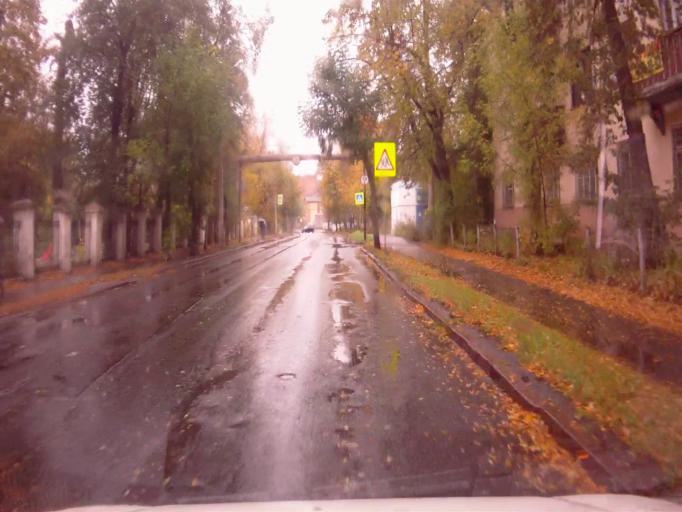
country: RU
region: Chelyabinsk
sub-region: Gorod Chelyabinsk
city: Chelyabinsk
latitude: 55.1931
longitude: 61.4115
